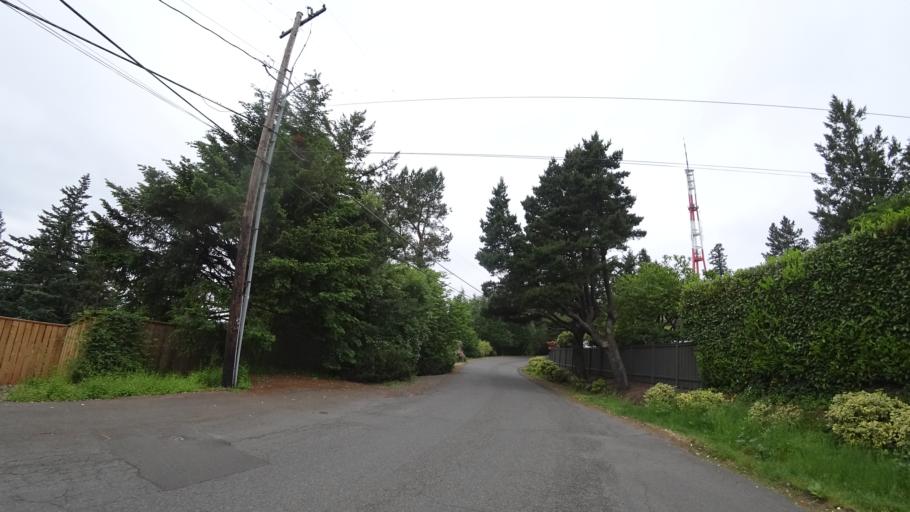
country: US
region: Oregon
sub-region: Multnomah County
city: Portland
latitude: 45.4865
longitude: -122.6939
